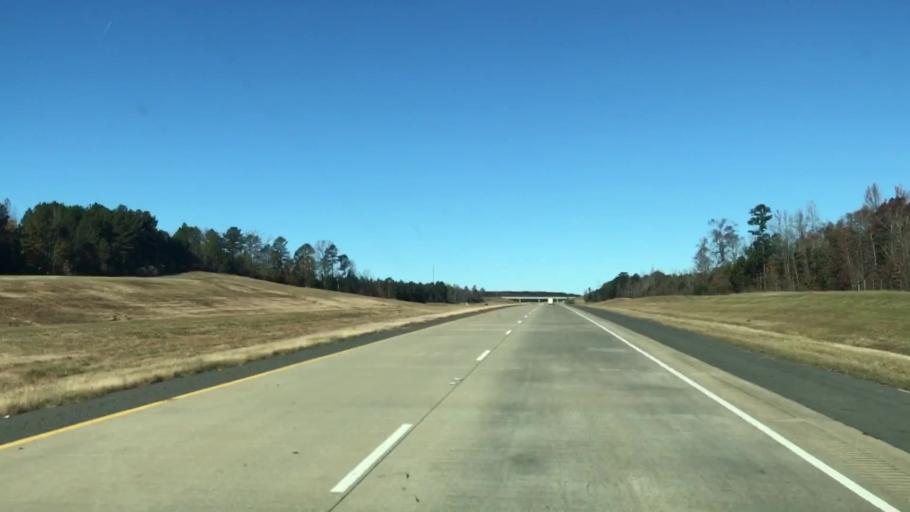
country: US
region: Louisiana
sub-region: Caddo Parish
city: Vivian
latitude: 32.9139
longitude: -93.8750
